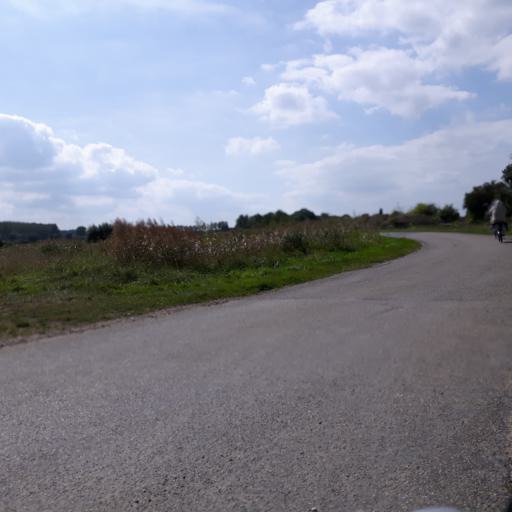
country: NL
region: Zeeland
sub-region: Gemeente Goes
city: Goes
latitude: 51.4657
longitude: 3.8974
